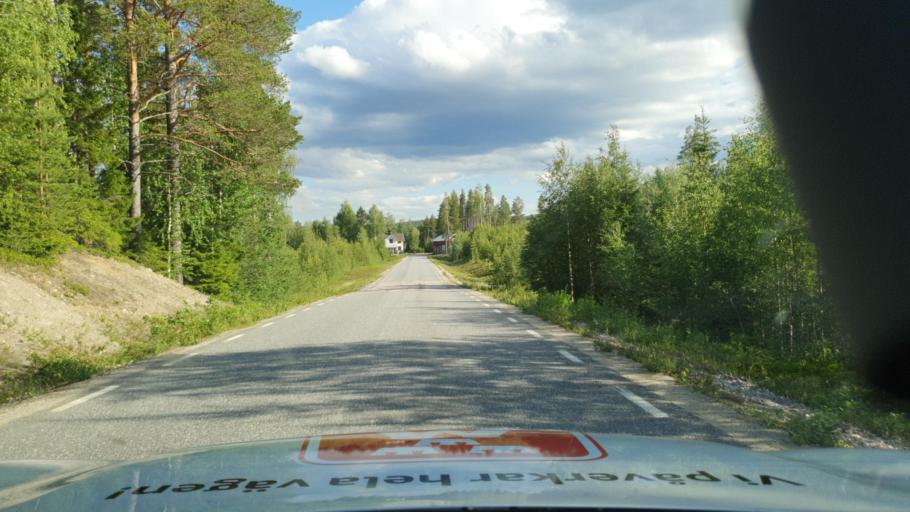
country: SE
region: Vaesterbotten
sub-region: Vindelns Kommun
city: Vindeln
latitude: 64.4986
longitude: 19.8005
